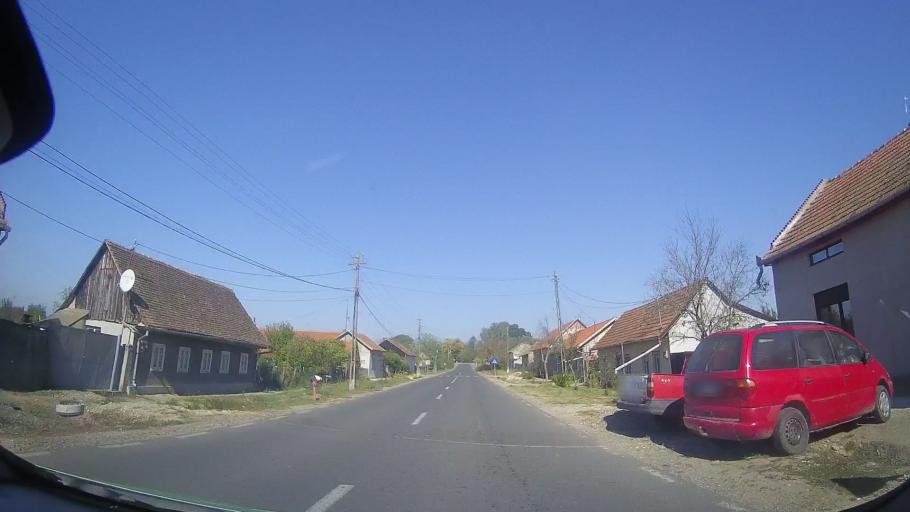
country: RO
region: Timis
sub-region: Comuna Balint
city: Balint
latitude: 45.8095
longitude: 21.8594
